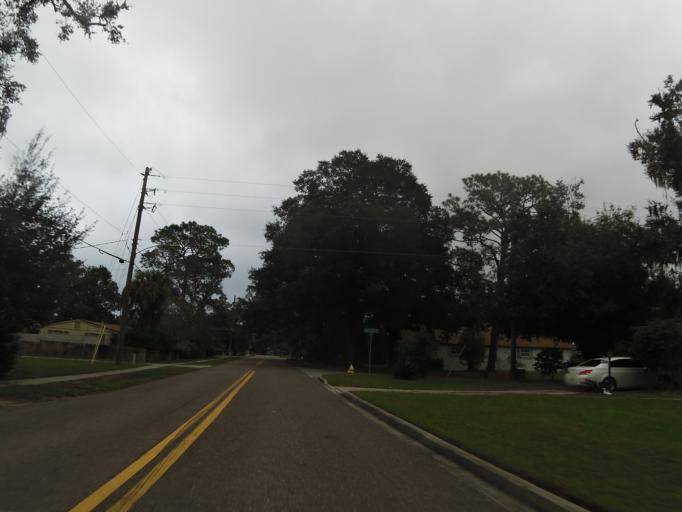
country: US
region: Florida
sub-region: Clay County
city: Bellair-Meadowbrook Terrace
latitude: 30.2724
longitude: -81.7397
